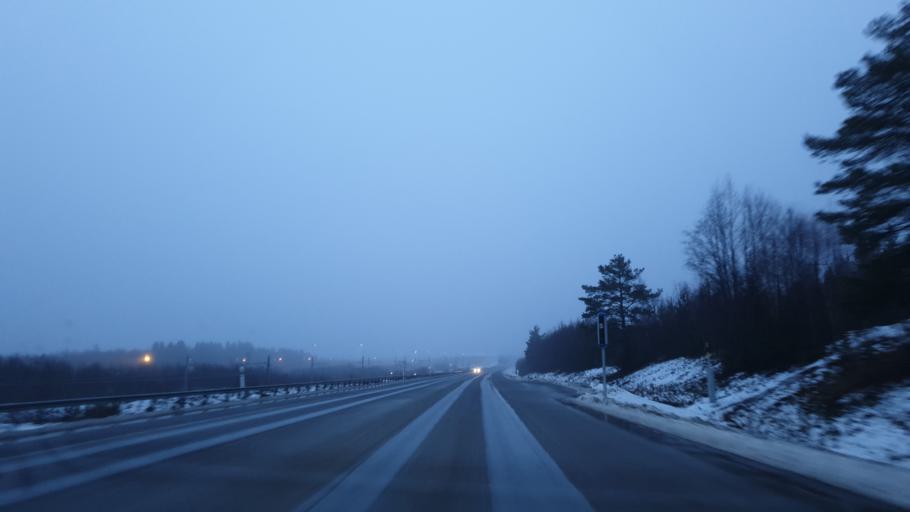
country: SE
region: Vaesterbotten
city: Obbola
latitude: 63.7794
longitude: 20.3245
